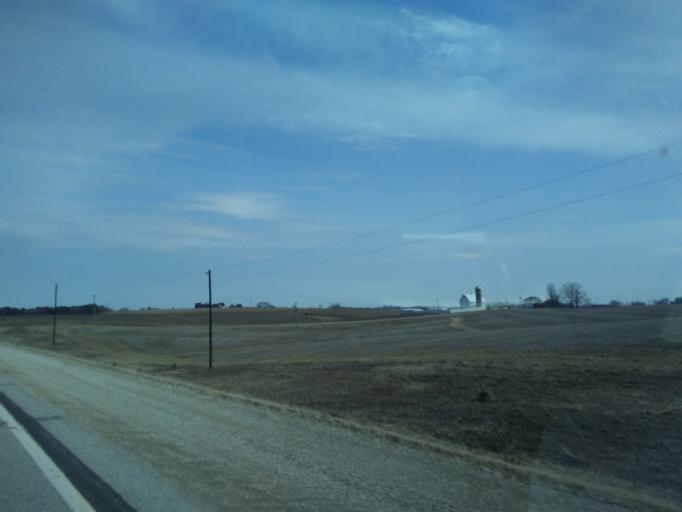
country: US
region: Iowa
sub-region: Allamakee County
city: Waukon
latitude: 43.2405
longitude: -91.5309
